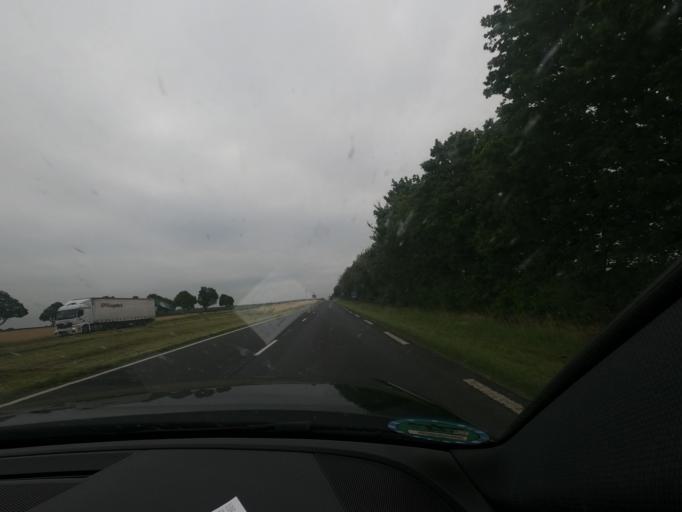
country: FR
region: Picardie
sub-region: Departement de la Somme
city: Harbonnieres
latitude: 49.7746
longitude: 2.6071
